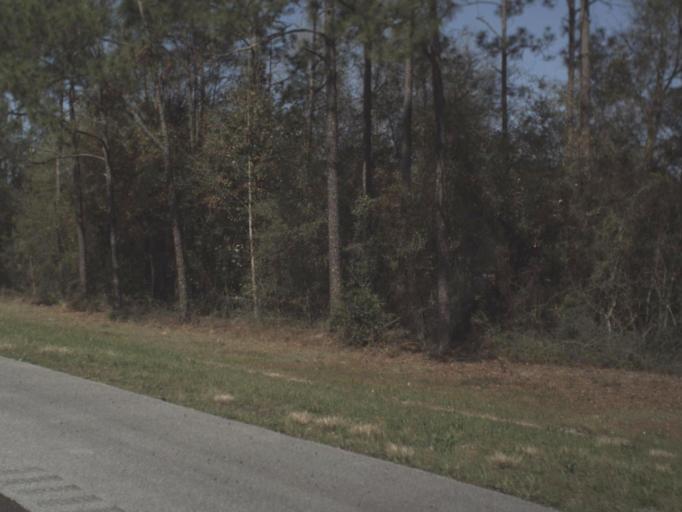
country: US
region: Florida
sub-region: Walton County
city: DeFuniak Springs
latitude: 30.7484
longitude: -86.2929
